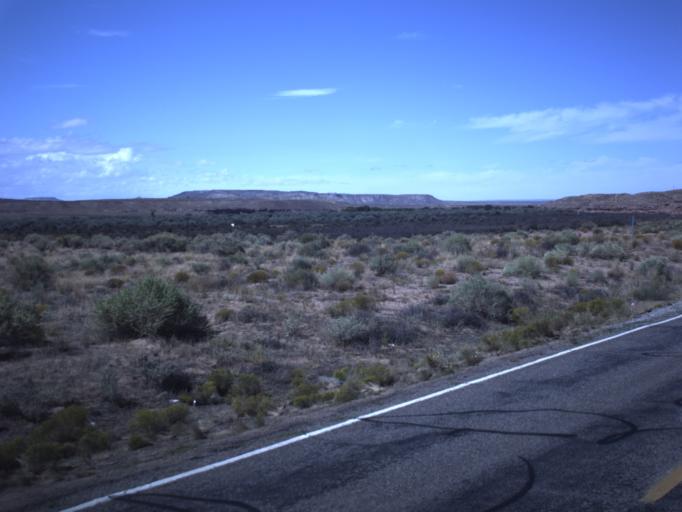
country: US
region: Utah
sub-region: San Juan County
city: Blanding
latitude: 37.2321
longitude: -109.2175
